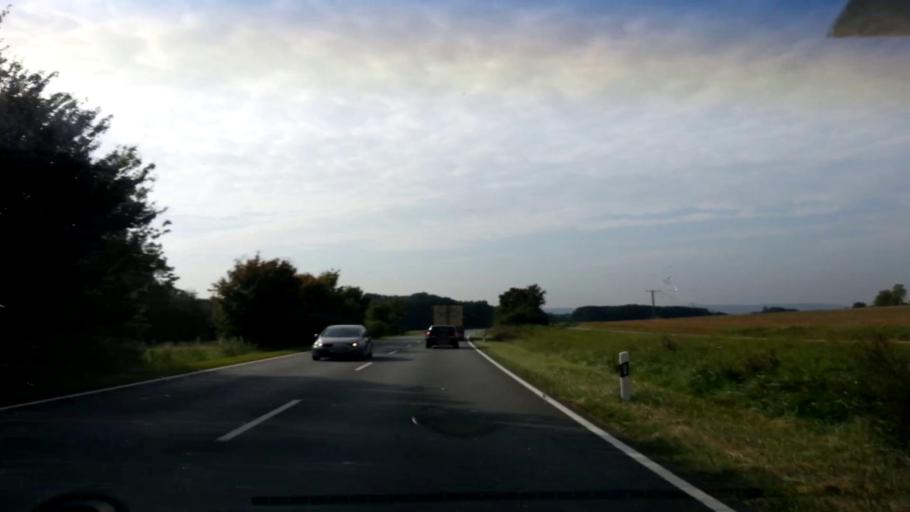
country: DE
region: Bavaria
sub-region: Regierungsbezirk Unterfranken
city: Prichsenstadt
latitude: 49.8068
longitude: 10.3610
